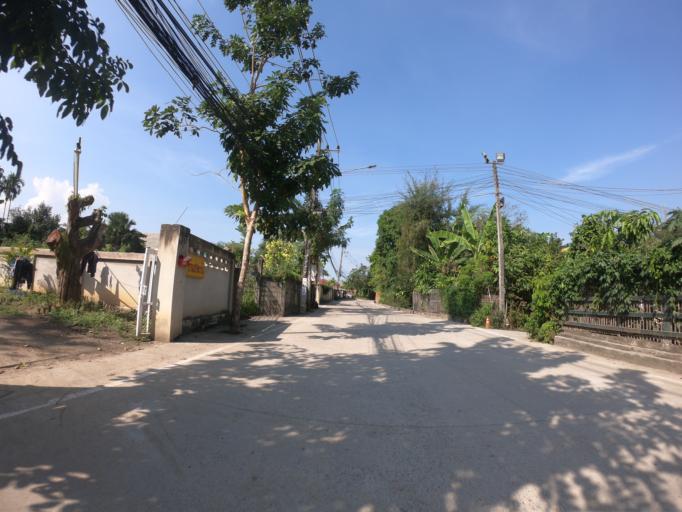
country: TH
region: Chiang Mai
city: Chiang Mai
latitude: 18.8197
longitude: 99.0065
